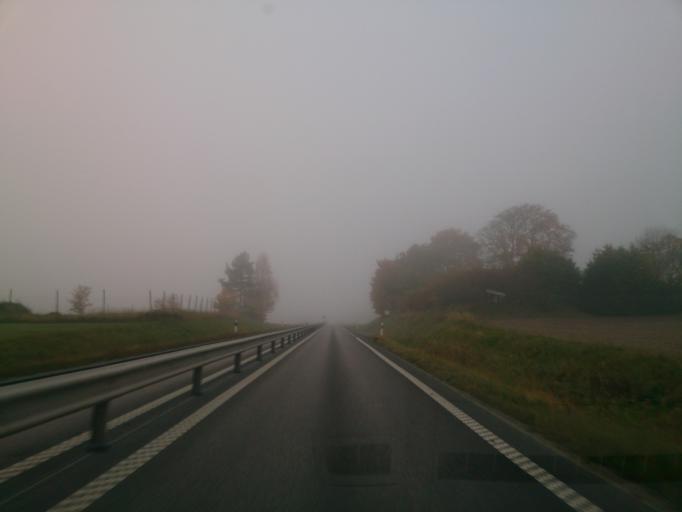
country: SE
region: OEstergoetland
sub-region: Kinda Kommun
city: Rimforsa
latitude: 58.1317
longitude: 15.6766
